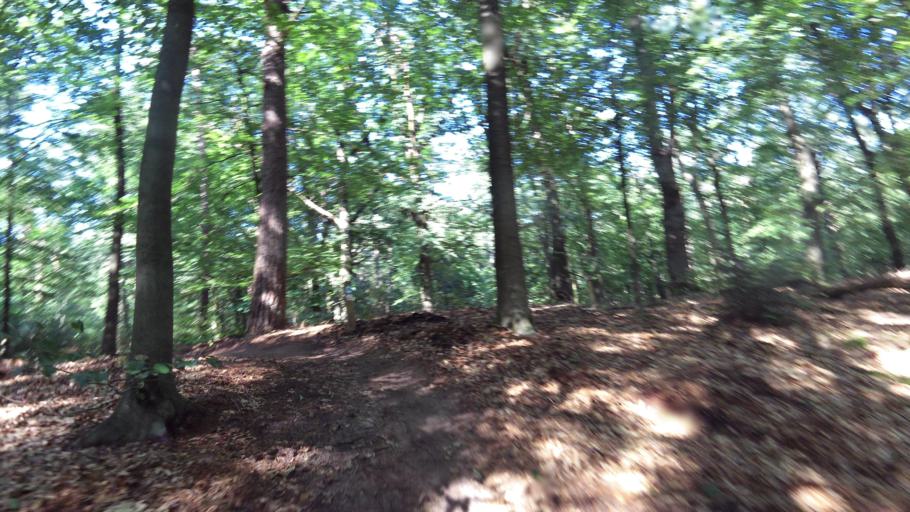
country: NL
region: Gelderland
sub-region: Gemeente Arnhem
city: Gulden Bodem
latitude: 52.0154
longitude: 5.9092
